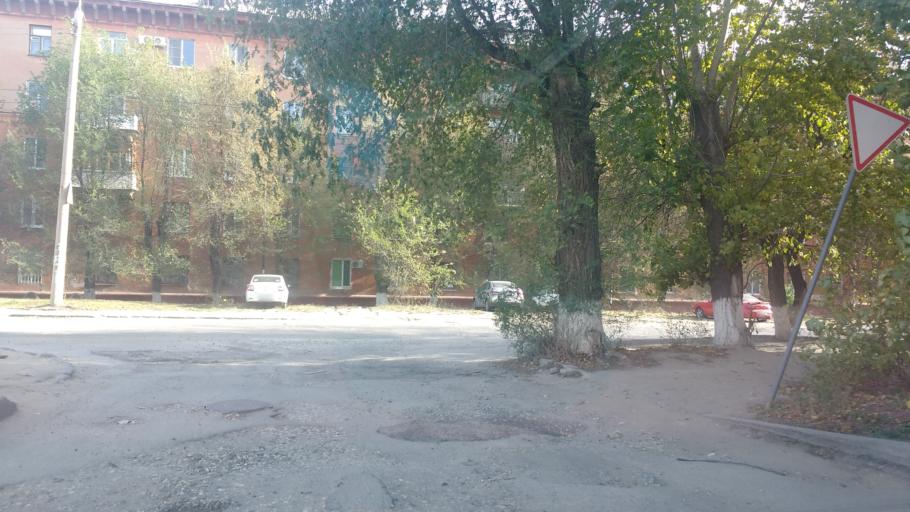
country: RU
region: Volgograd
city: Krasnoslobodsk
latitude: 48.7608
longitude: 44.5531
